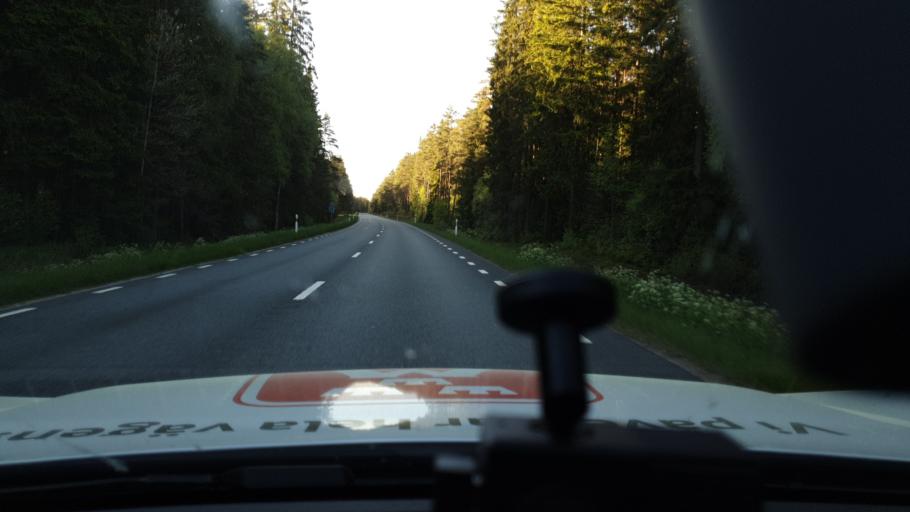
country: SE
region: Joenkoeping
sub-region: Vetlanda Kommun
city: Ekenassjon
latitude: 57.5790
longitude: 14.9714
